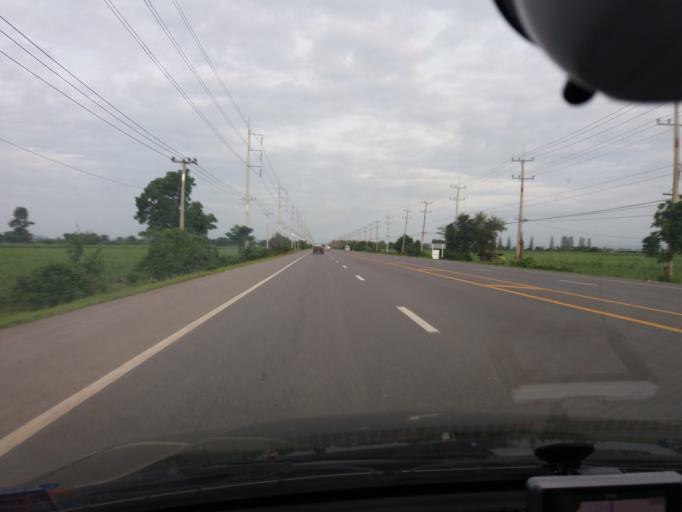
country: TH
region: Suphan Buri
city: U Thong
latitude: 14.3366
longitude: 99.8199
